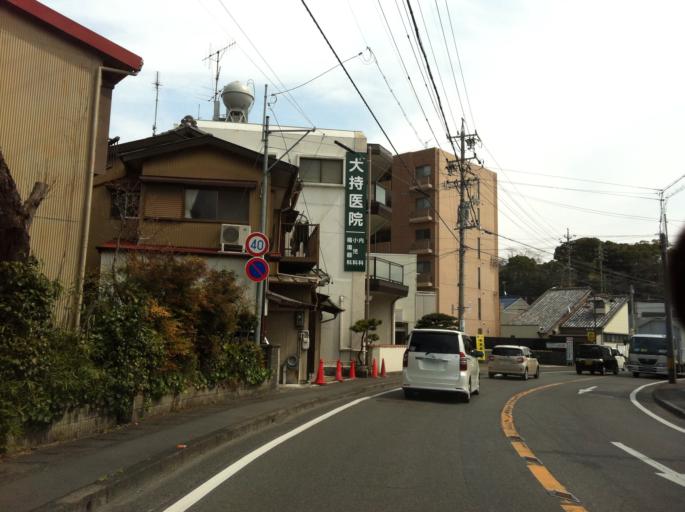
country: JP
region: Shizuoka
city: Fujieda
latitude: 34.8716
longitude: 138.2544
